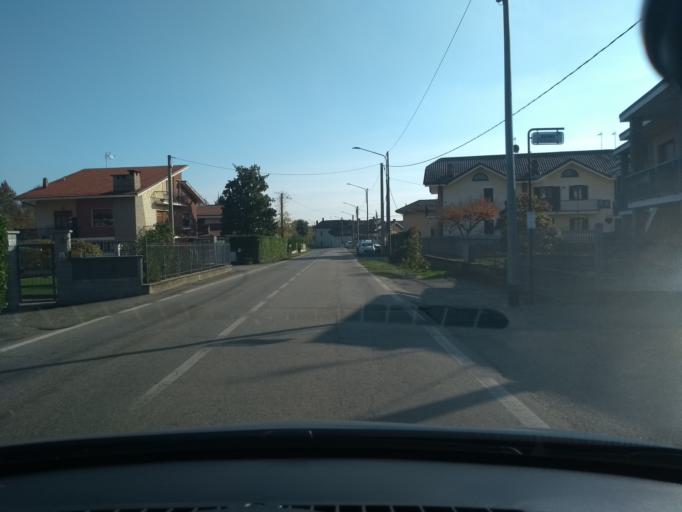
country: IT
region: Piedmont
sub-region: Provincia di Torino
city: Fiano
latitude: 45.2151
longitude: 7.5377
